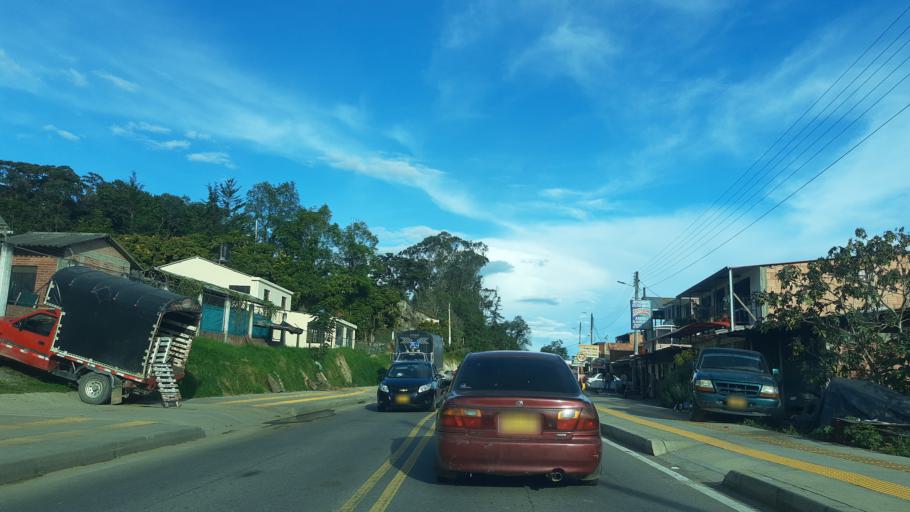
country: CO
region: Cundinamarca
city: Macheta
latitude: 5.0786
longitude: -73.6074
